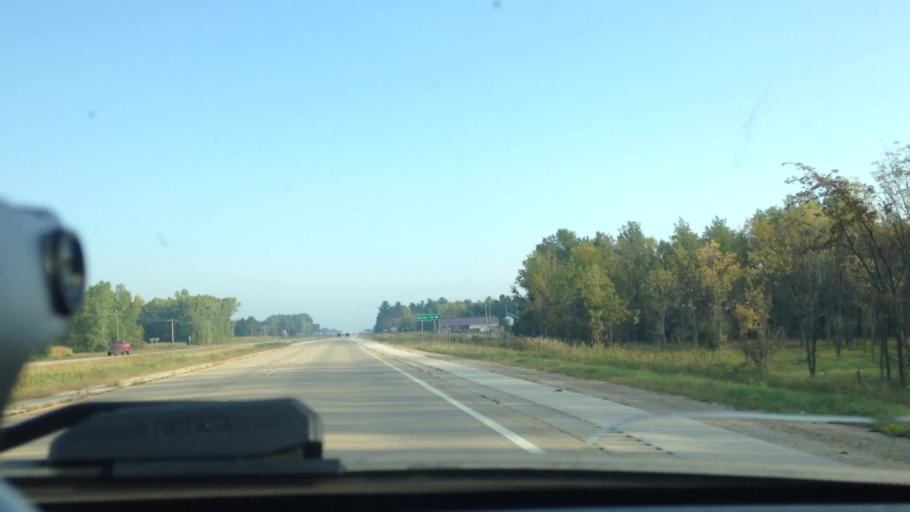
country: US
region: Wisconsin
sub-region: Oconto County
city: Oconto Falls
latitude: 45.0197
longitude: -88.0449
